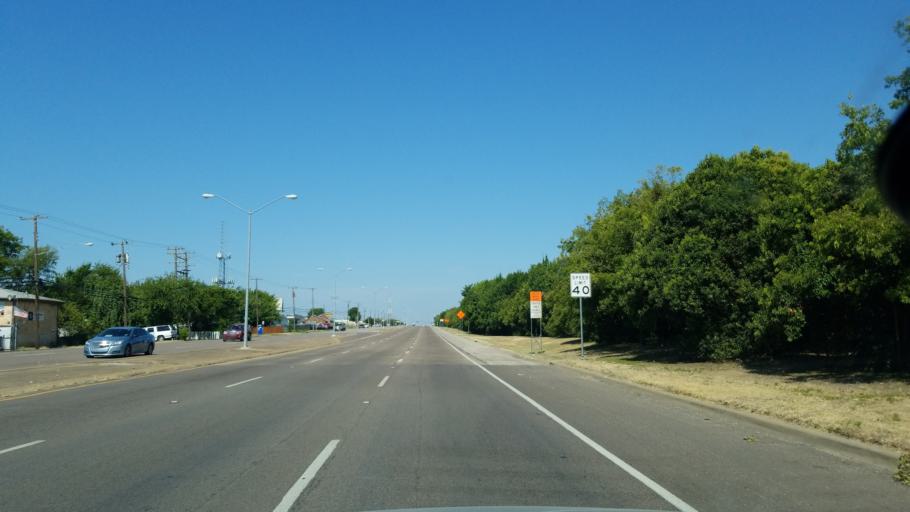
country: US
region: Texas
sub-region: Dallas County
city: Cockrell Hill
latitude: 32.7497
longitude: -96.8839
